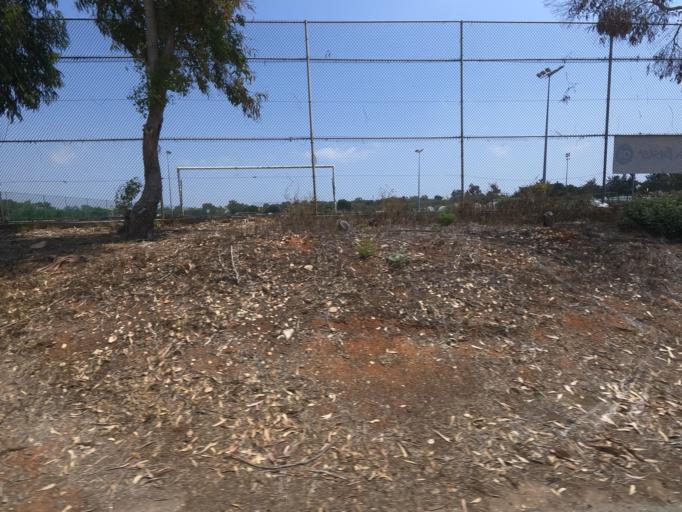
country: CY
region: Ammochostos
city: Ayia Napa
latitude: 34.9936
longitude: 34.0089
